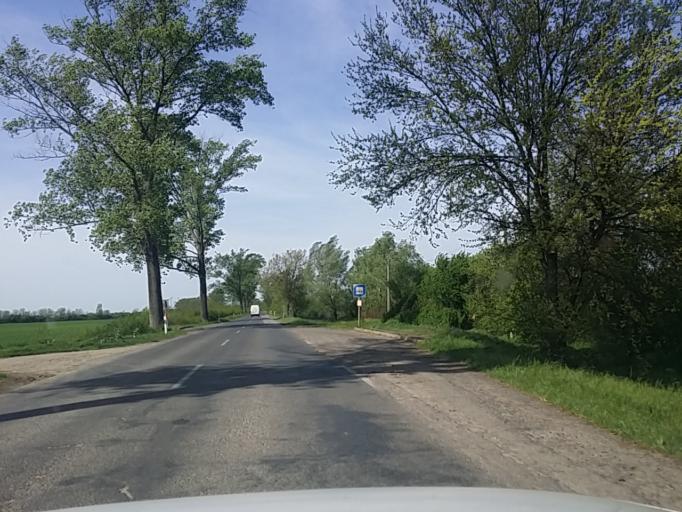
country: HU
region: Bekes
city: Doboz
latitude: 46.7166
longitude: 21.1943
